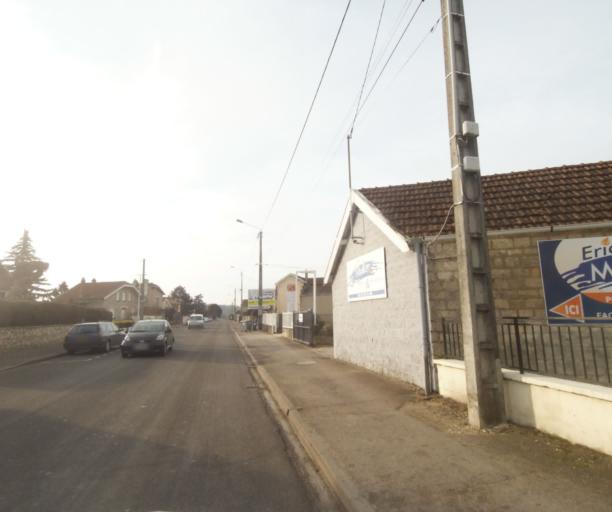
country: FR
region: Champagne-Ardenne
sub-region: Departement de la Haute-Marne
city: Saint-Dizier
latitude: 48.6322
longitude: 4.9352
